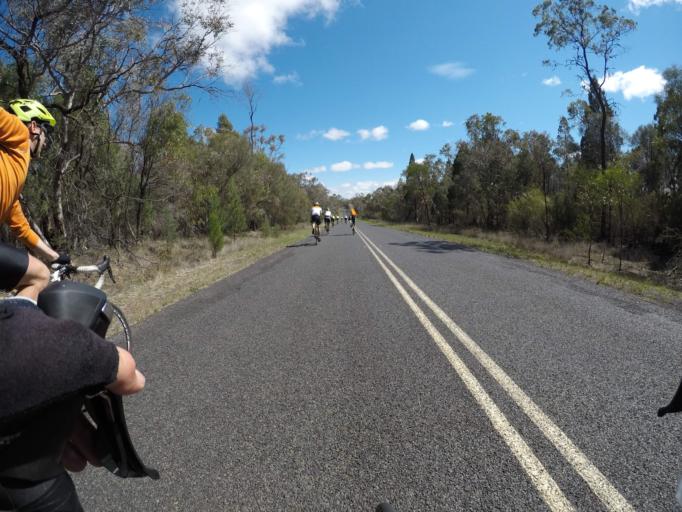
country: AU
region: New South Wales
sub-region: Dubbo Municipality
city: Eulomogo
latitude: -32.6019
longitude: 148.5451
